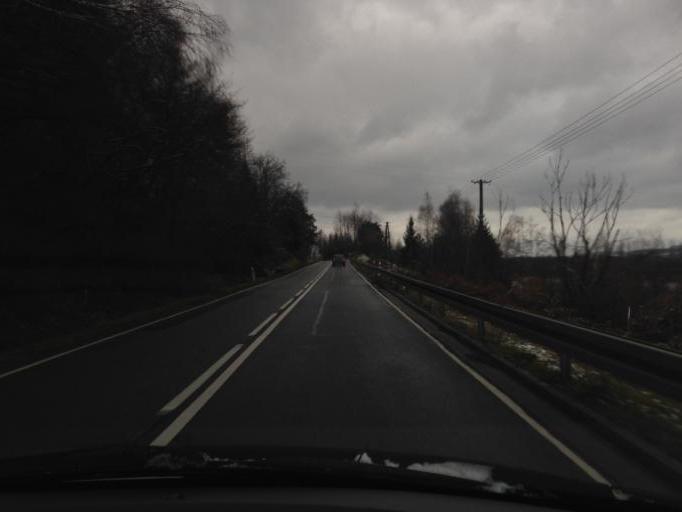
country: PL
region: Lesser Poland Voivodeship
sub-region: Powiat tarnowski
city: Zakliczyn
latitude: 49.8667
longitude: 20.7962
